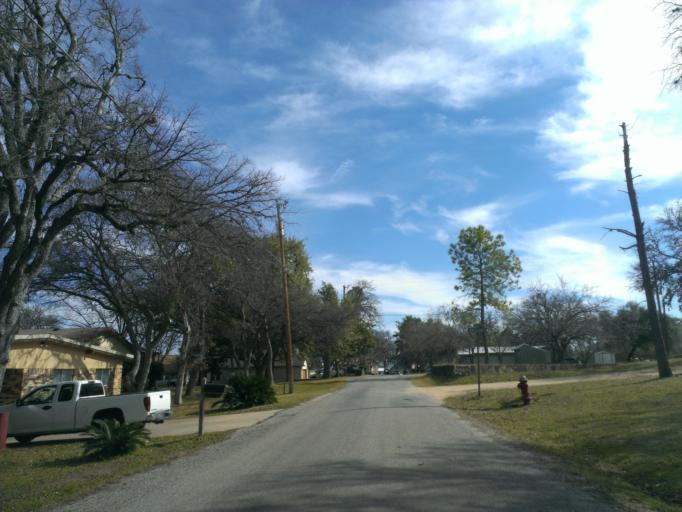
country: US
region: Texas
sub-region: Burnet County
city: Granite Shoals
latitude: 30.5780
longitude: -98.3889
